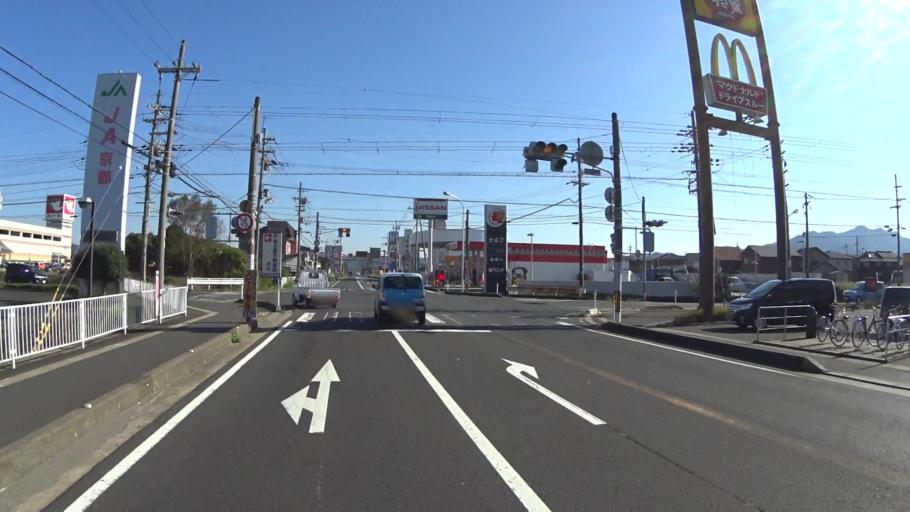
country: JP
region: Kyoto
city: Miyazu
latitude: 35.6089
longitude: 135.0803
